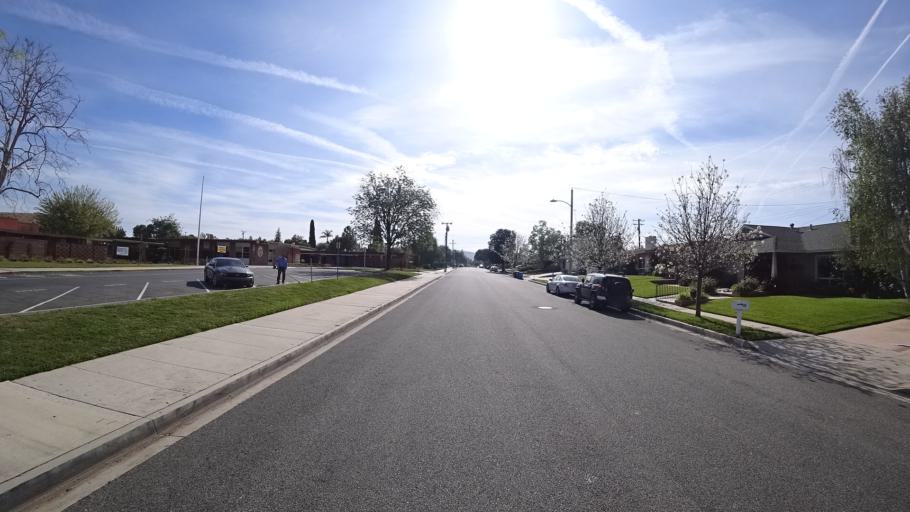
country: US
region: California
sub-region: Ventura County
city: Thousand Oaks
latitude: 34.1968
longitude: -118.8770
